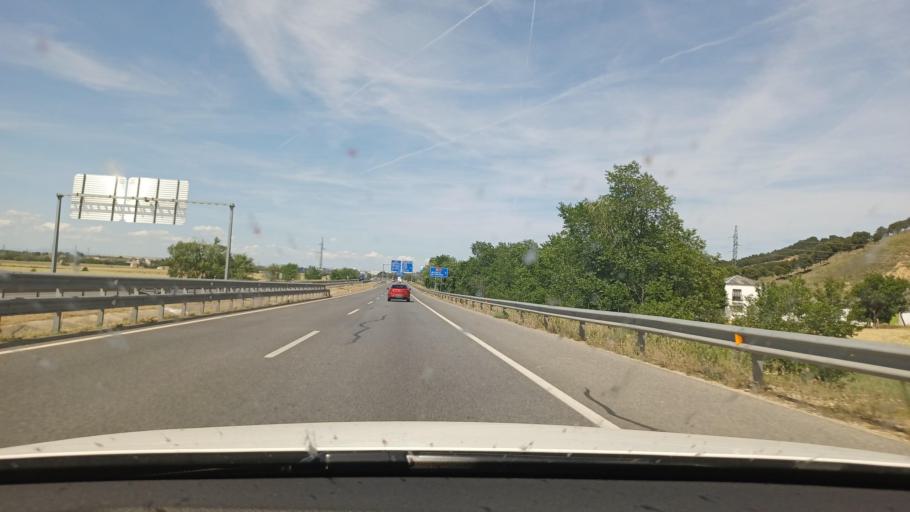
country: ES
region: Madrid
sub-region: Provincia de Madrid
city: Torrejon de Ardoz
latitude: 40.4532
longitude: -3.4184
